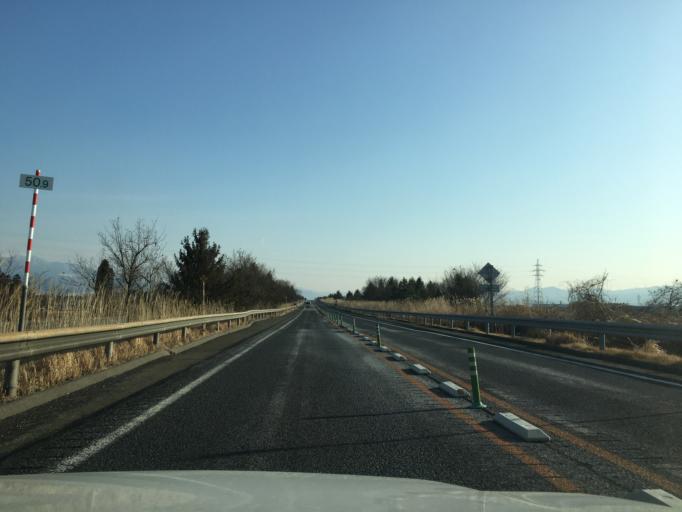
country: JP
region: Yamagata
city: Sagae
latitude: 38.3436
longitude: 140.2972
